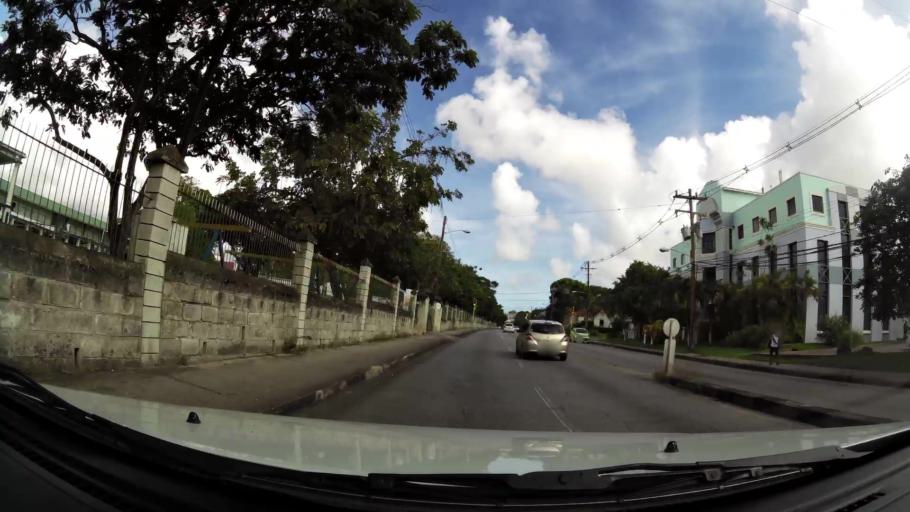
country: BB
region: Saint Michael
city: Bridgetown
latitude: 13.0932
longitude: -59.6056
